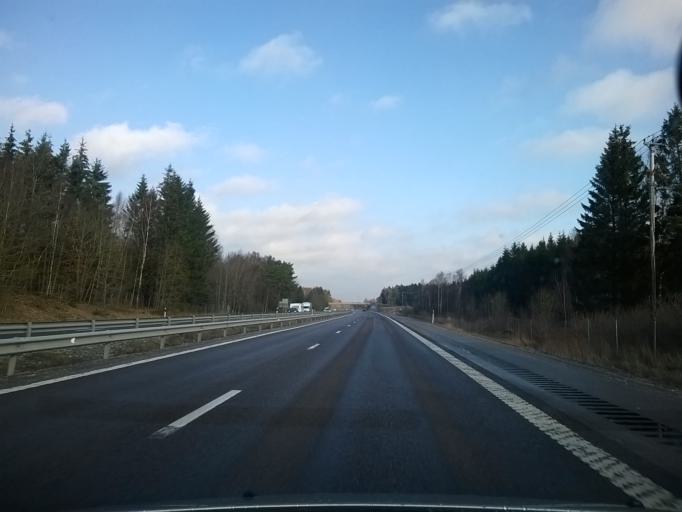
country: SE
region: Vaestra Goetaland
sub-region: Kungalvs Kommun
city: Kode
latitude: 57.9573
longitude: 11.8484
